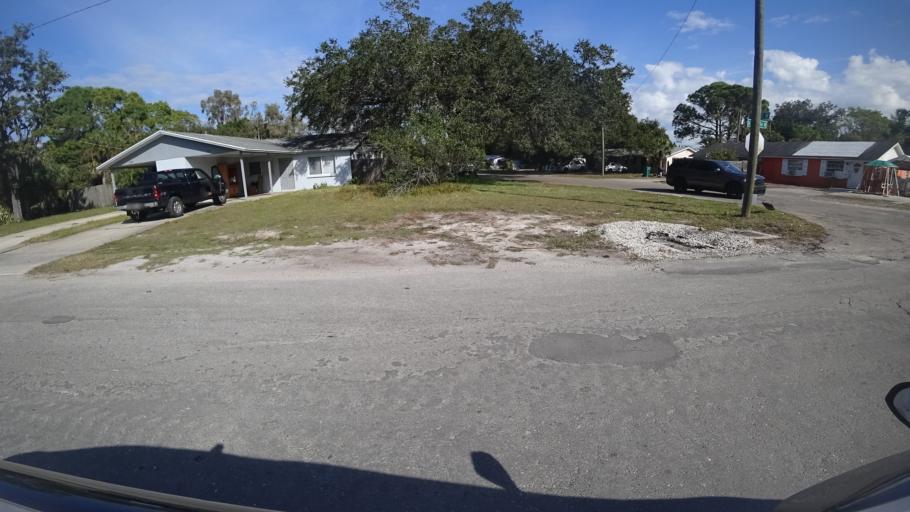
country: US
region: Florida
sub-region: Manatee County
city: Whitfield
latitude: 27.4335
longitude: -82.5693
